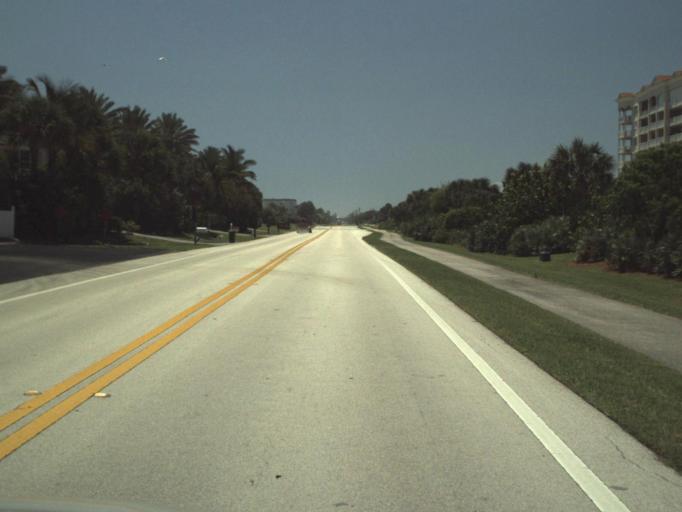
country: US
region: Florida
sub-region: Brevard County
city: Micco
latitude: 27.9261
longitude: -80.4852
